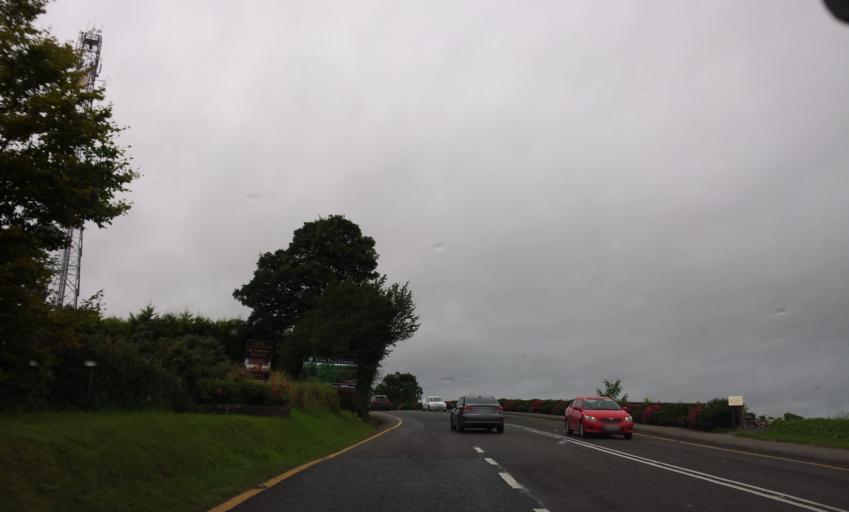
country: IE
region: Munster
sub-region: County Cork
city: Mitchelstown
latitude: 52.2461
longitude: -8.4223
